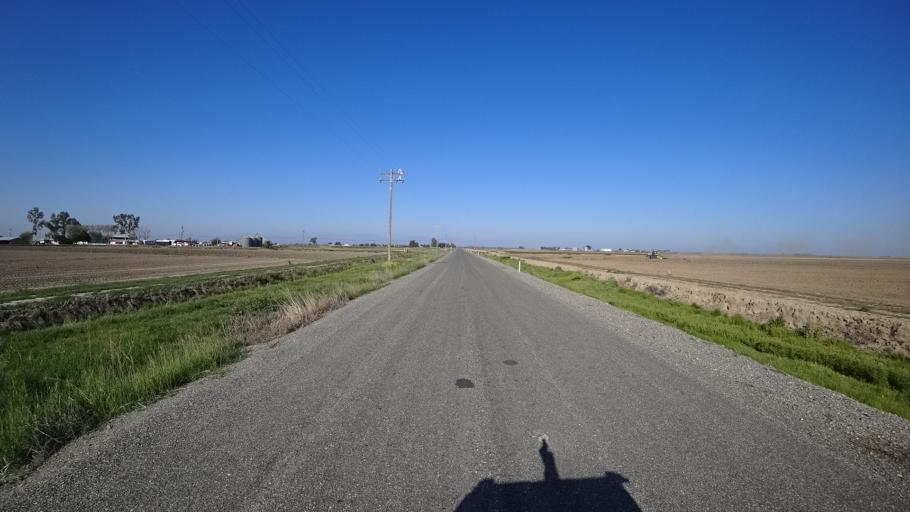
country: US
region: California
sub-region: Glenn County
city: Willows
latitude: 39.5385
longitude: -122.1102
